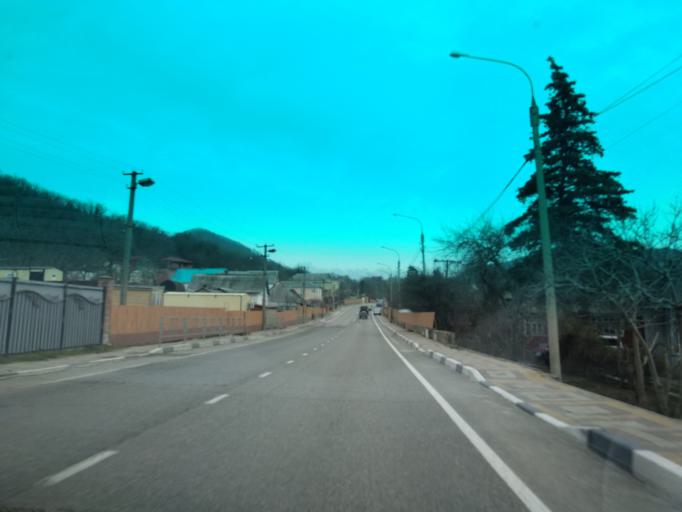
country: RU
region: Krasnodarskiy
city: Ol'ginka
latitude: 44.2089
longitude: 38.8919
